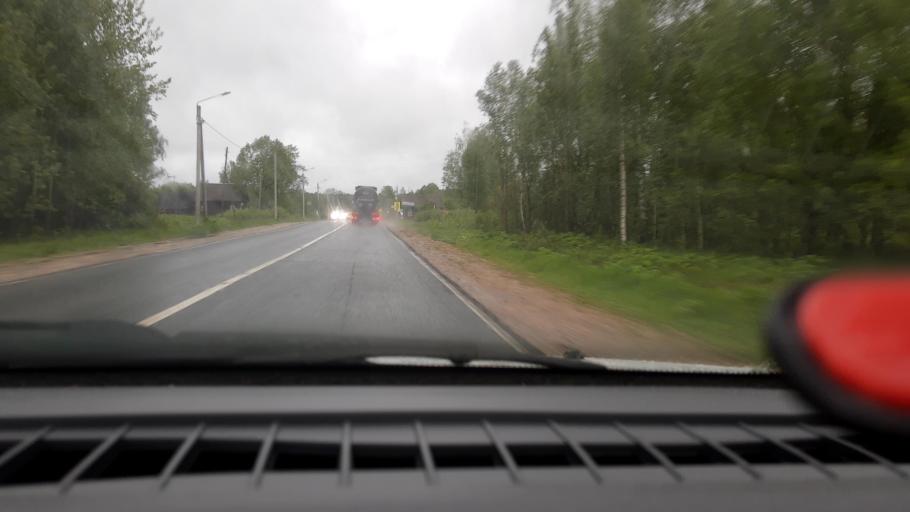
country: RU
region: Nizjnij Novgorod
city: Sukhobezvodnoye
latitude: 56.8680
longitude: 44.9295
